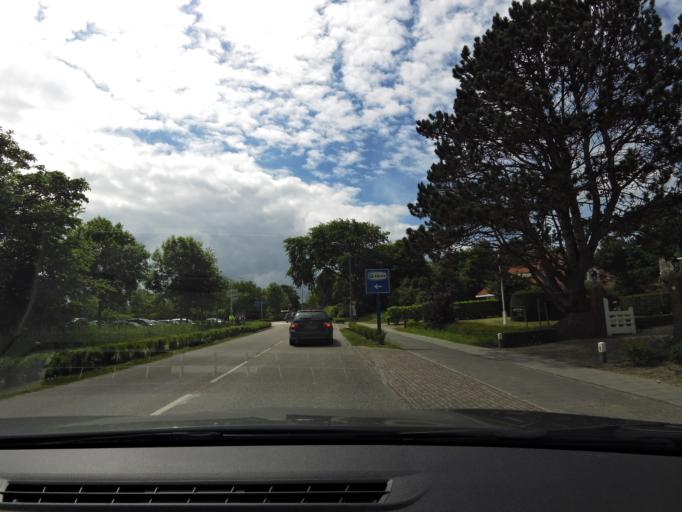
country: NL
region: Zeeland
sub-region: Gemeente Middelburg
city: Middelburg
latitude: 51.5653
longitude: 3.5051
